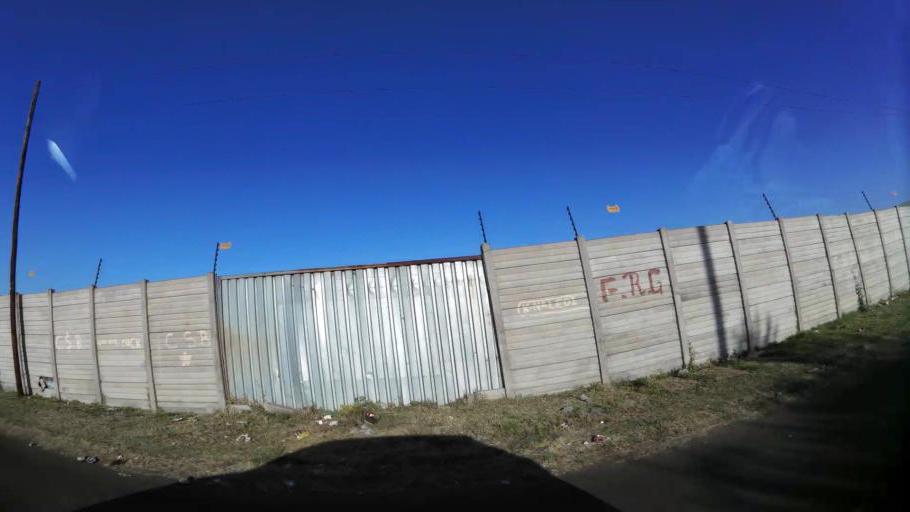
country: ZA
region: North-West
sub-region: Bojanala Platinum District Municipality
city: Rustenburg
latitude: -25.6338
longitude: 27.2215
